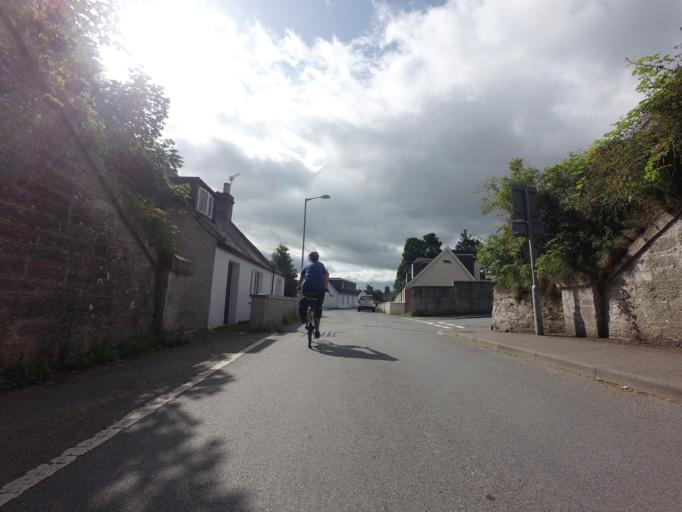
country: GB
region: Scotland
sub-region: Highland
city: Nairn
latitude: 57.5818
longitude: -3.8665
